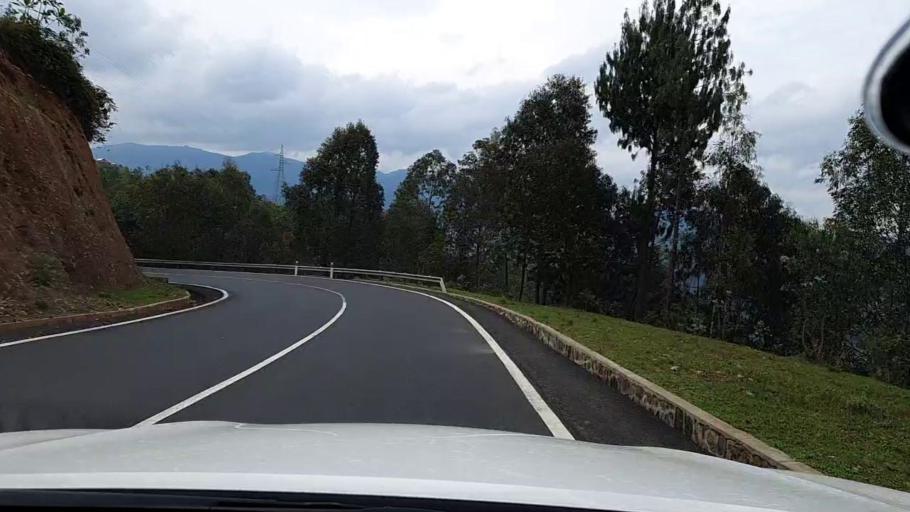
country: RW
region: Western Province
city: Kibuye
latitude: -2.1789
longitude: 29.2888
